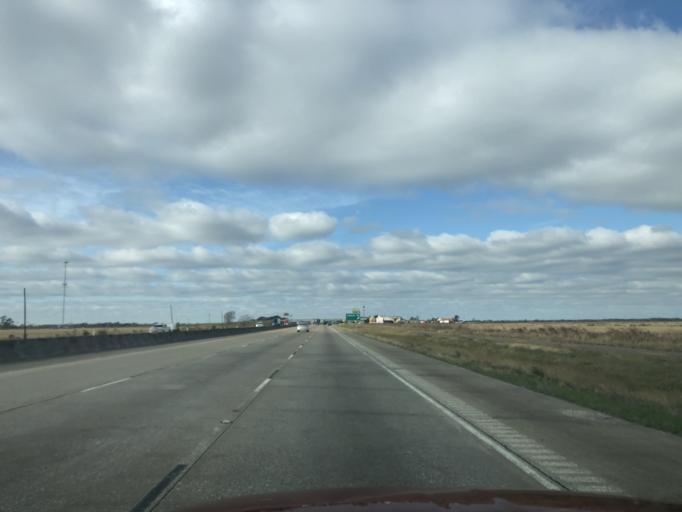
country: US
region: Texas
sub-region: Chambers County
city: Winnie
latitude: 29.8343
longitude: -94.5325
